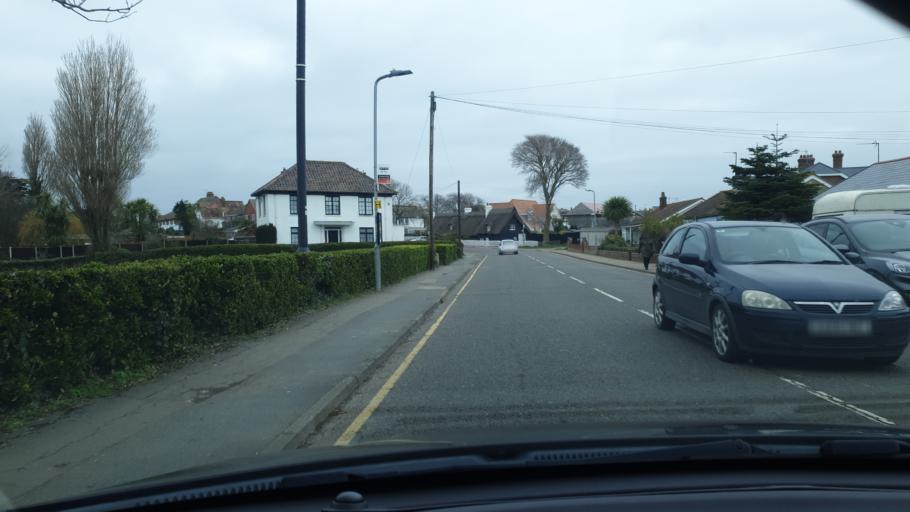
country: GB
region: England
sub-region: Essex
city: Walton-on-the-Naze
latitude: 51.8543
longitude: 1.2785
